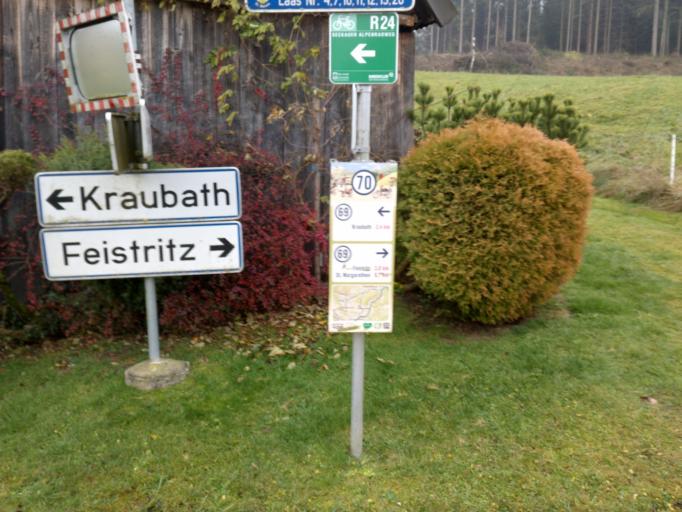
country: AT
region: Styria
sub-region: Politischer Bezirk Murtal
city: Feistritz bei Knittelfeld
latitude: 47.2908
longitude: 14.9017
